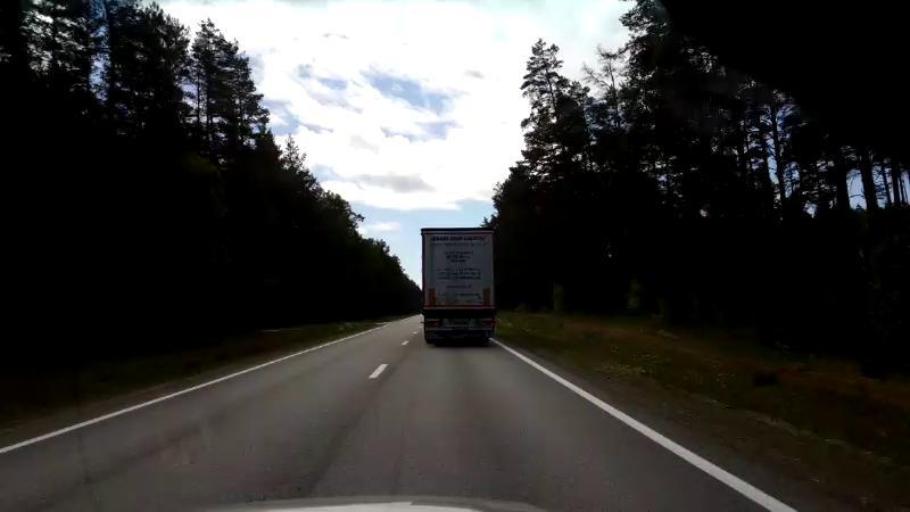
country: LV
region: Salacgrivas
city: Salacgriva
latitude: 57.5199
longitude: 24.4307
